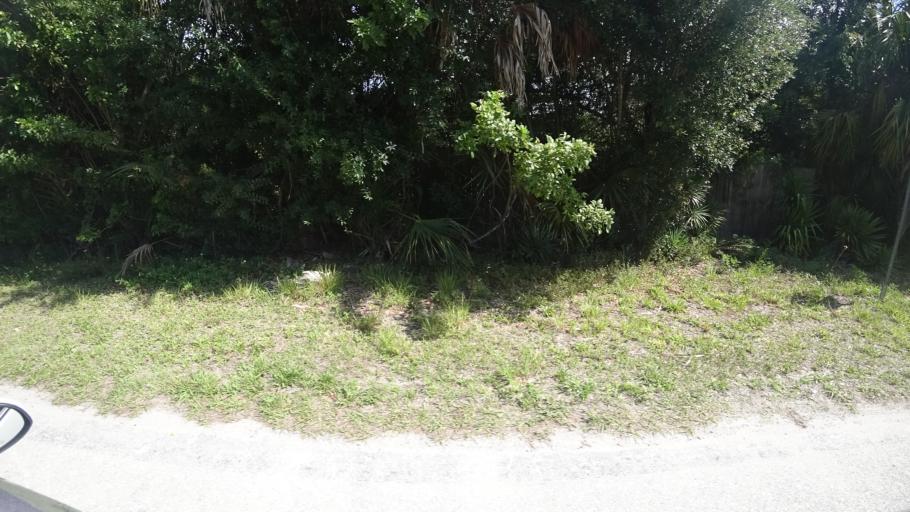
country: US
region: Florida
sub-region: Manatee County
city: Whitfield
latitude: 27.4111
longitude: -82.5284
